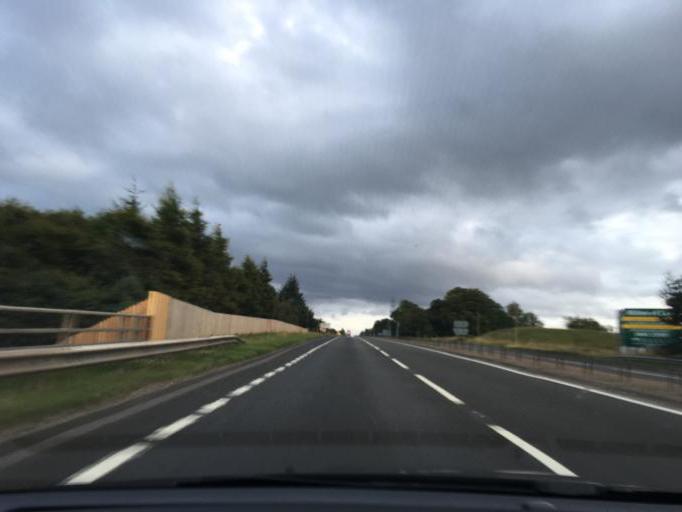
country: GB
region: Scotland
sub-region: Highland
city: Inverness
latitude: 57.4532
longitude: -4.1606
